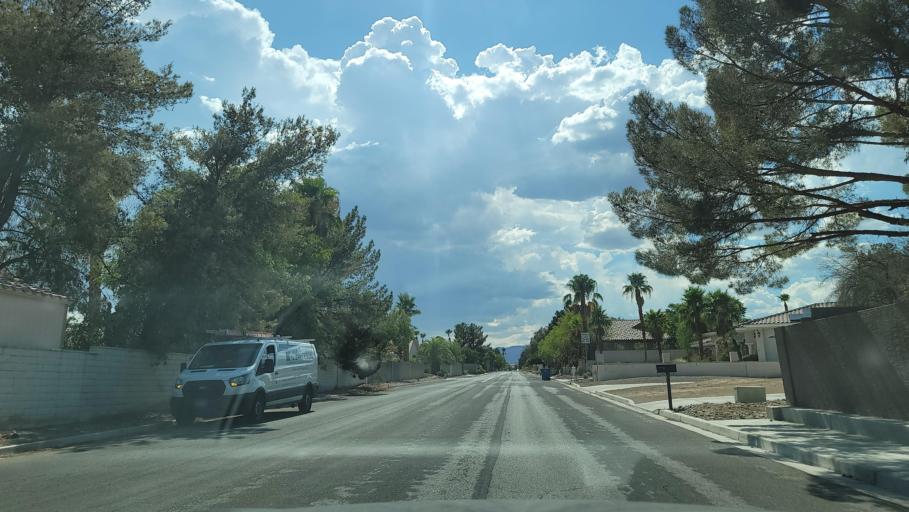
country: US
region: Nevada
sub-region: Clark County
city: Spring Valley
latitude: 36.1312
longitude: -115.2526
